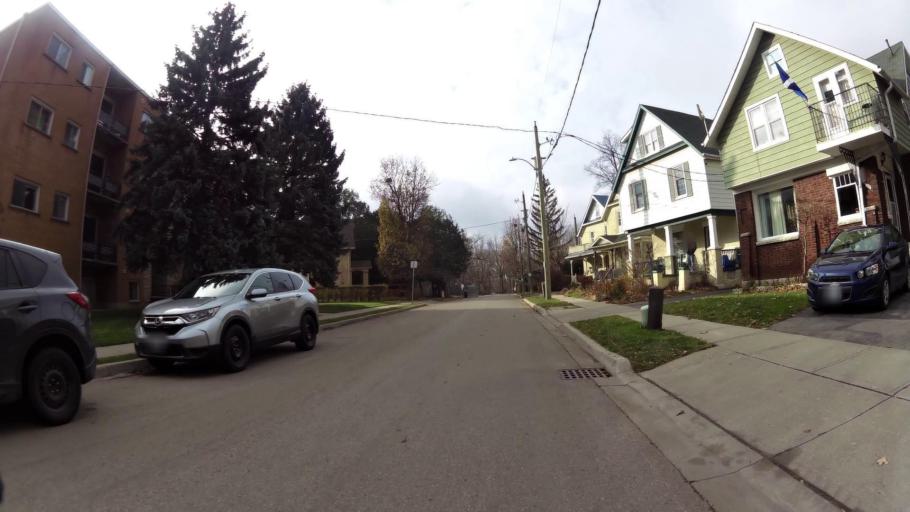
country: CA
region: Ontario
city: Kitchener
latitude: 43.4446
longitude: -80.4969
